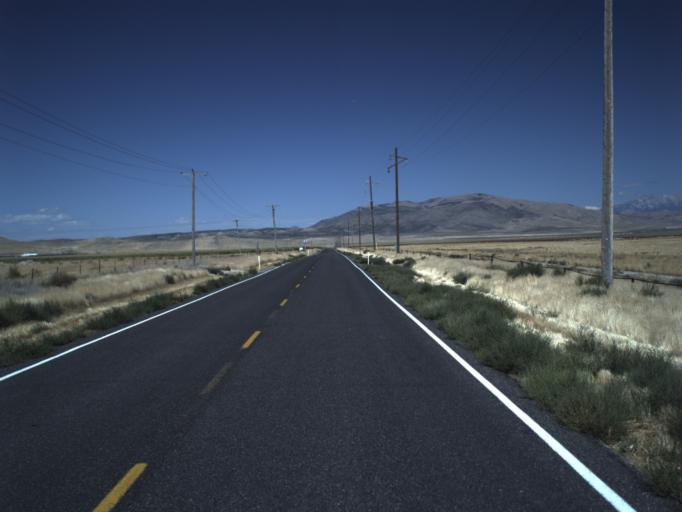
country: US
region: Utah
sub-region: Utah County
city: Genola
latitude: 40.0817
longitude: -111.9587
